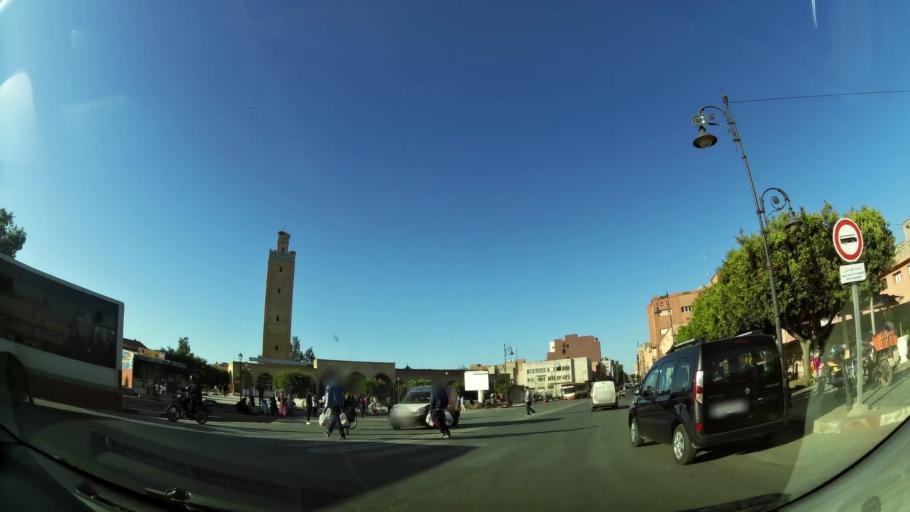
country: MA
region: Oriental
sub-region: Berkane-Taourirt
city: Berkane
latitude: 34.9223
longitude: -2.3377
